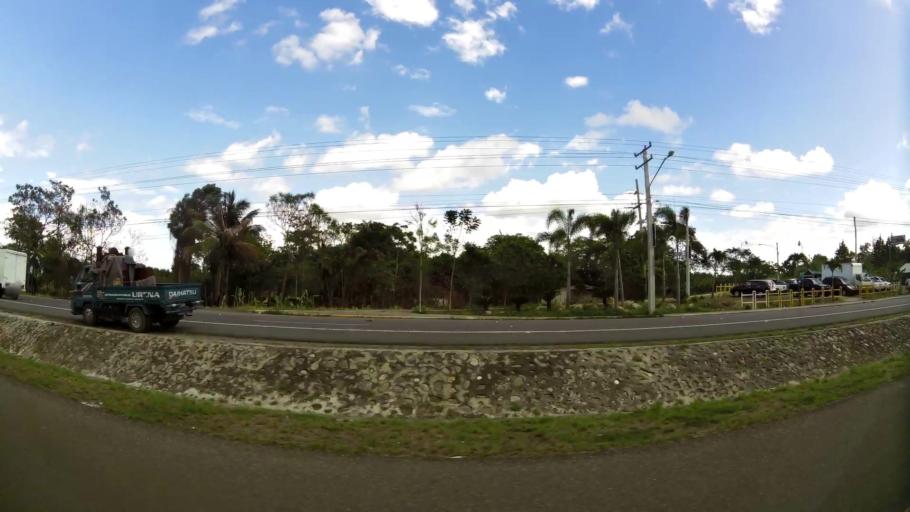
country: DO
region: La Vega
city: Rio Verde Arriba
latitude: 19.3472
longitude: -70.6002
